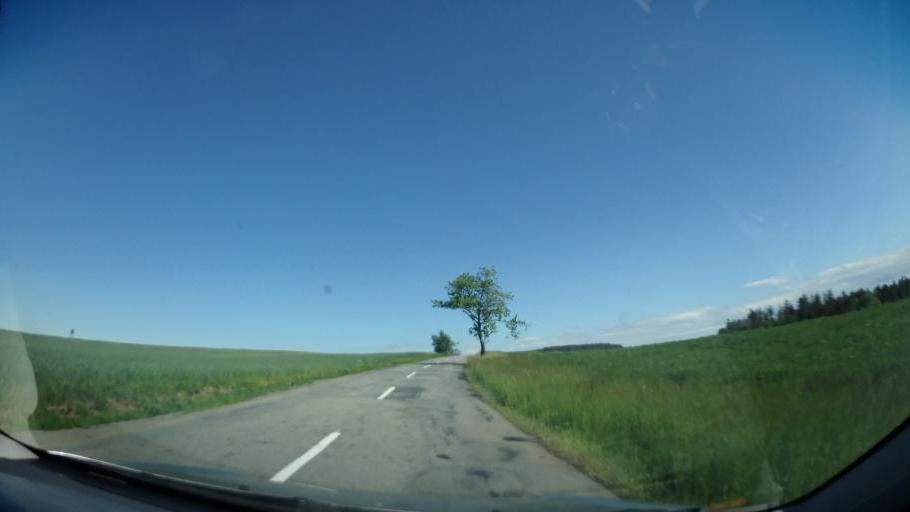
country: CZ
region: South Moravian
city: Velke Opatovice
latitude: 49.6178
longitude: 16.6070
